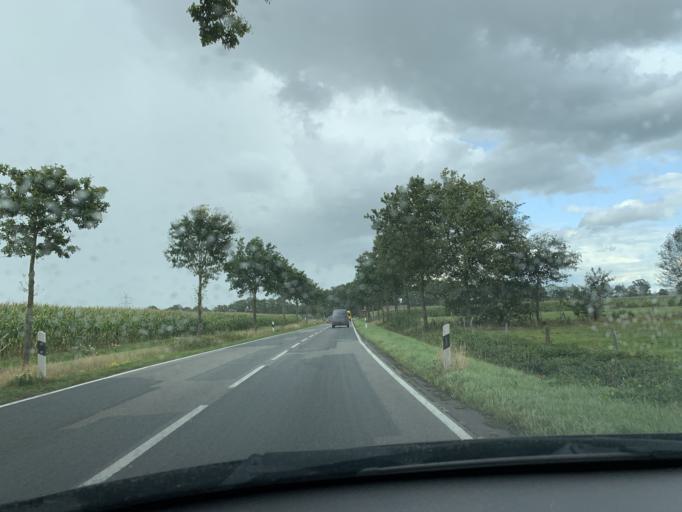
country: DE
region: Lower Saxony
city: Wiefelstede
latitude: 53.2926
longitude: 8.0377
